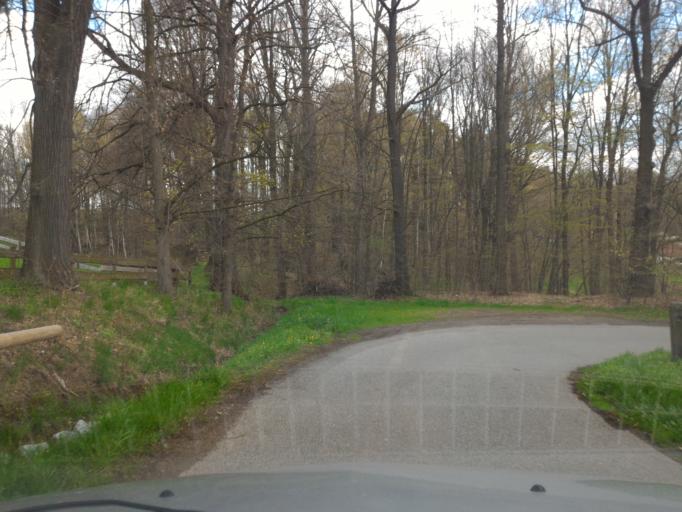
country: DE
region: Saxony
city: Hainewalde
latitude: 50.9168
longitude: 14.7073
